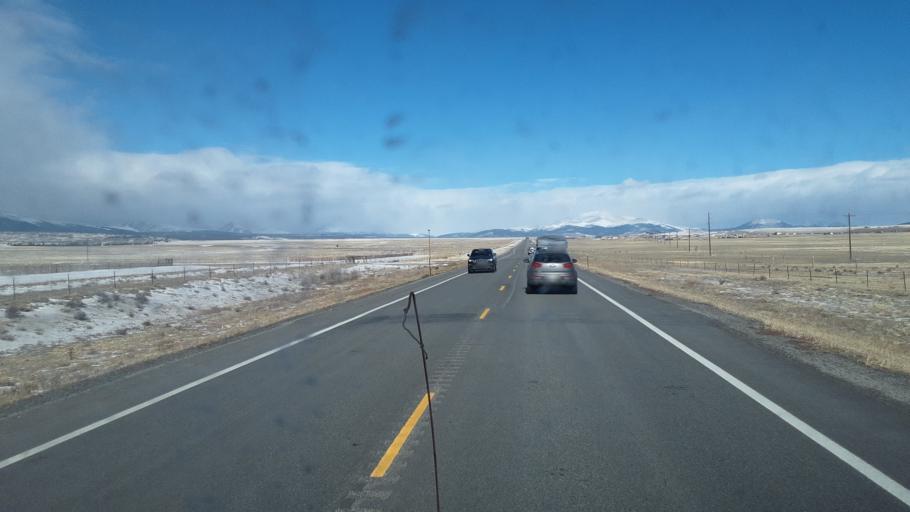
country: US
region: Colorado
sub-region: Park County
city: Fairplay
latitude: 39.1039
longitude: -105.9898
